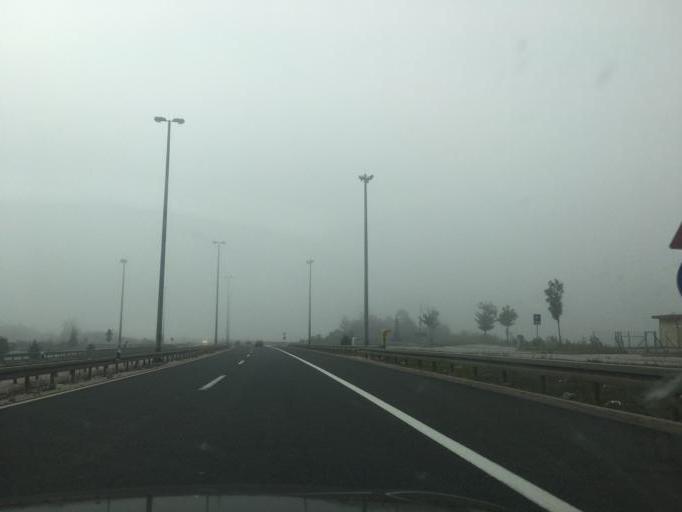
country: HR
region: Licko-Senjska
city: Gospic
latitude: 44.6253
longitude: 15.4382
